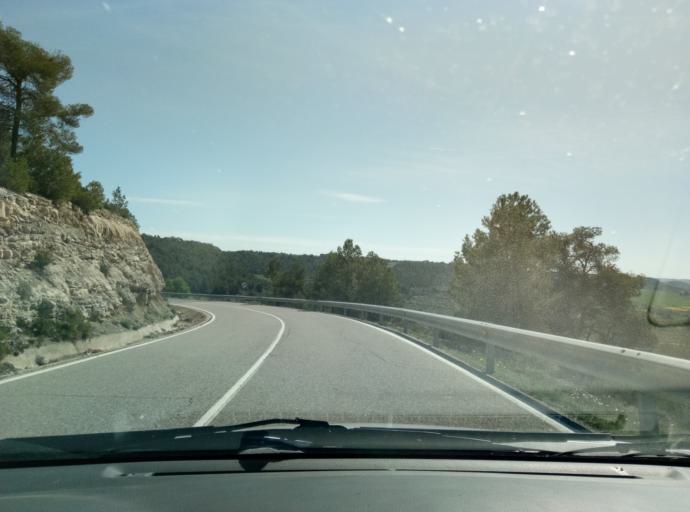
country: ES
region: Catalonia
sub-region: Provincia de Lleida
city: Vallbona de les Monges
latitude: 41.5270
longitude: 1.0269
